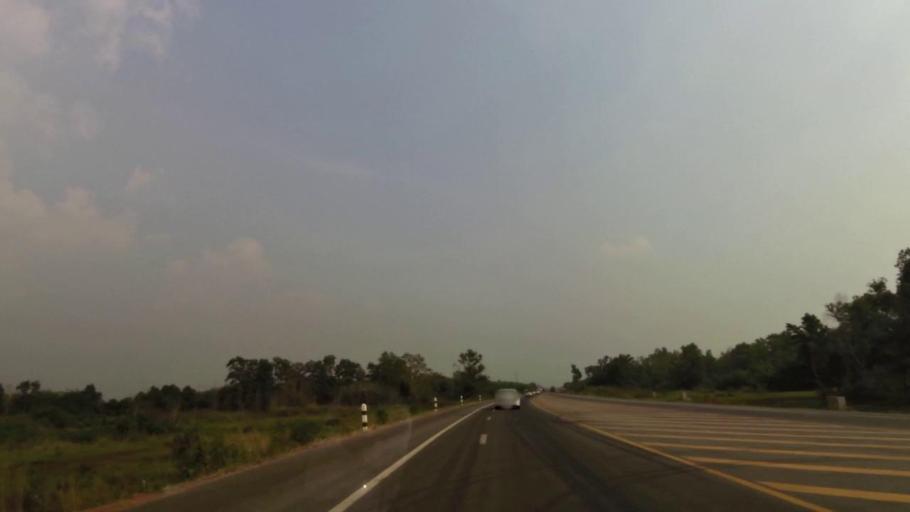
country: TH
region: Rayong
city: Klaeng
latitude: 12.8078
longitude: 101.6489
